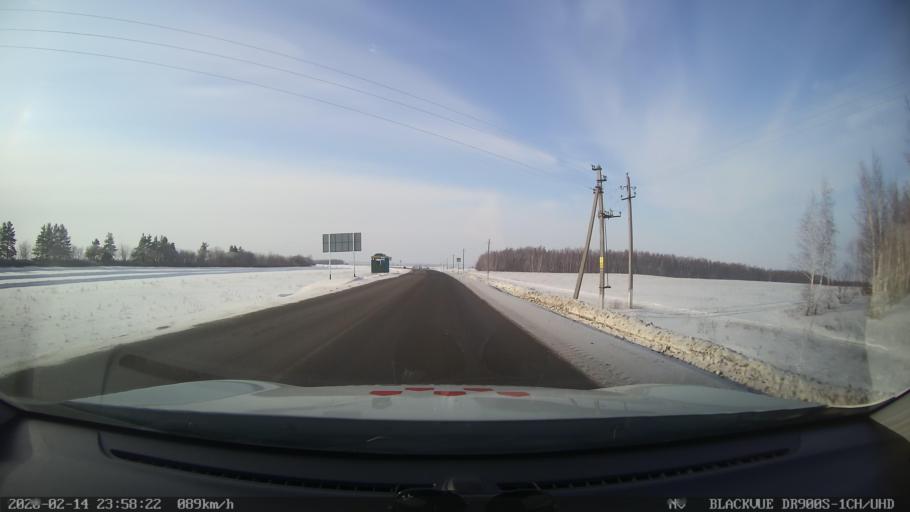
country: RU
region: Tatarstan
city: Kuybyshevskiy Zaton
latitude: 55.3403
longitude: 49.0889
